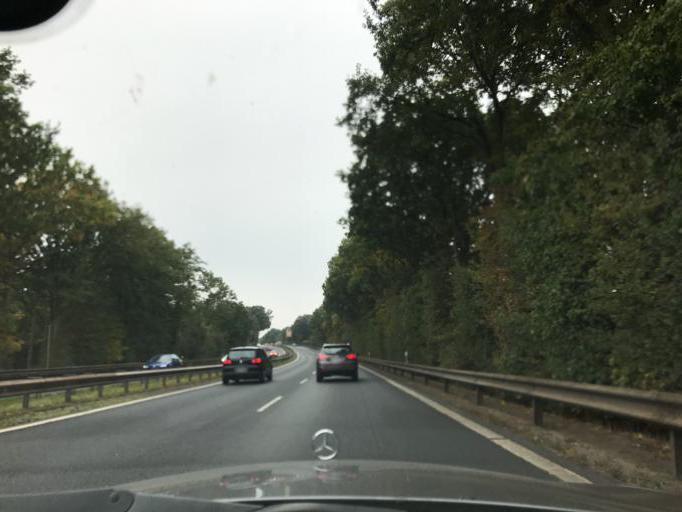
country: DE
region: Bremen
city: Bremen
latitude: 53.0324
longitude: 8.8562
